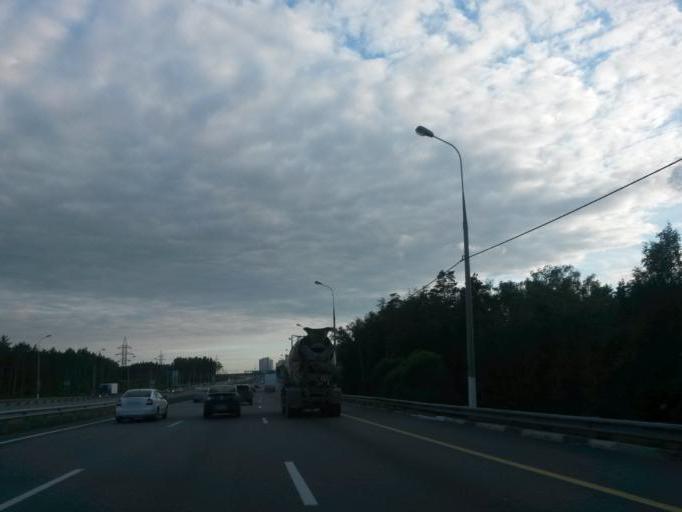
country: RU
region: Moskovskaya
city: Vostryakovo
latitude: 55.4108
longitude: 37.7908
